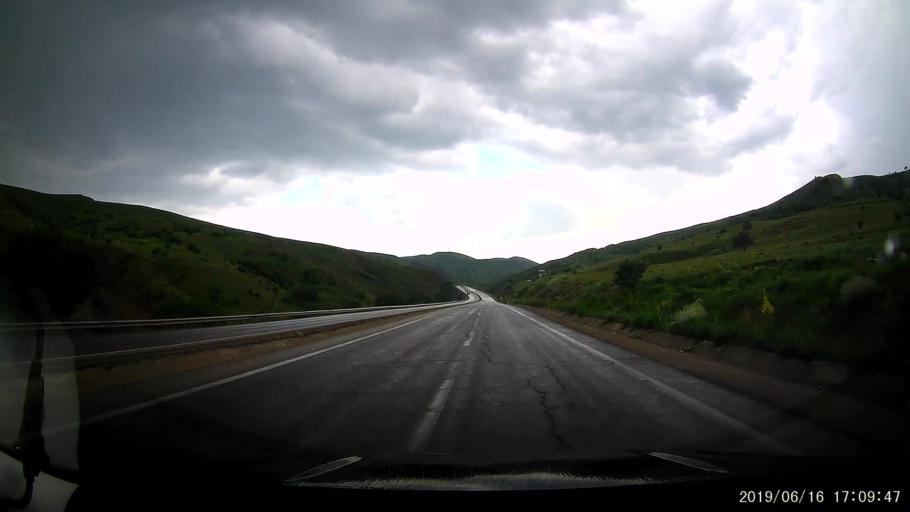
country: TR
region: Erzurum
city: Askale
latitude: 39.8894
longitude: 40.6479
